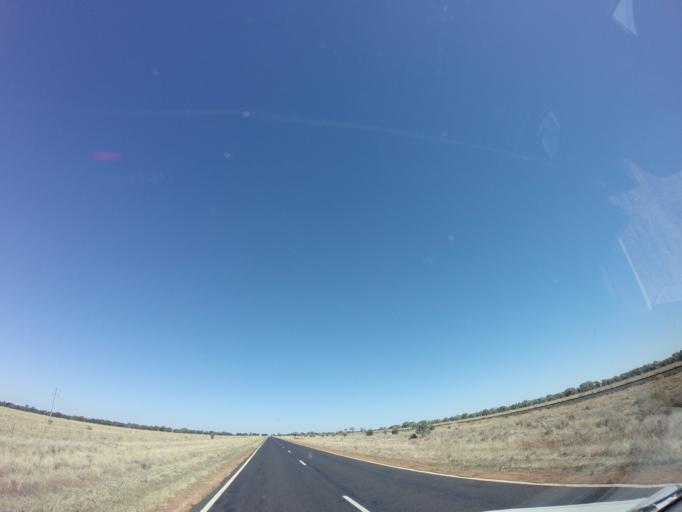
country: AU
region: New South Wales
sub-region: Bogan
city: Nyngan
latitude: -31.6768
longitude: 147.4131
